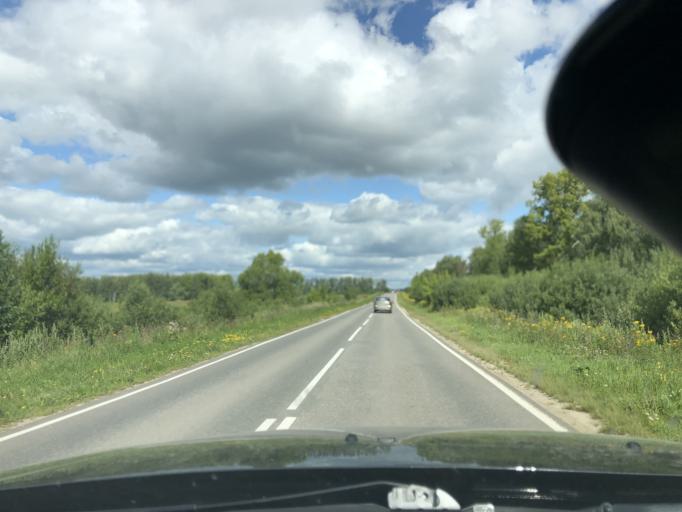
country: RU
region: Tula
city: Yasnogorsk
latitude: 54.4561
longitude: 37.7114
